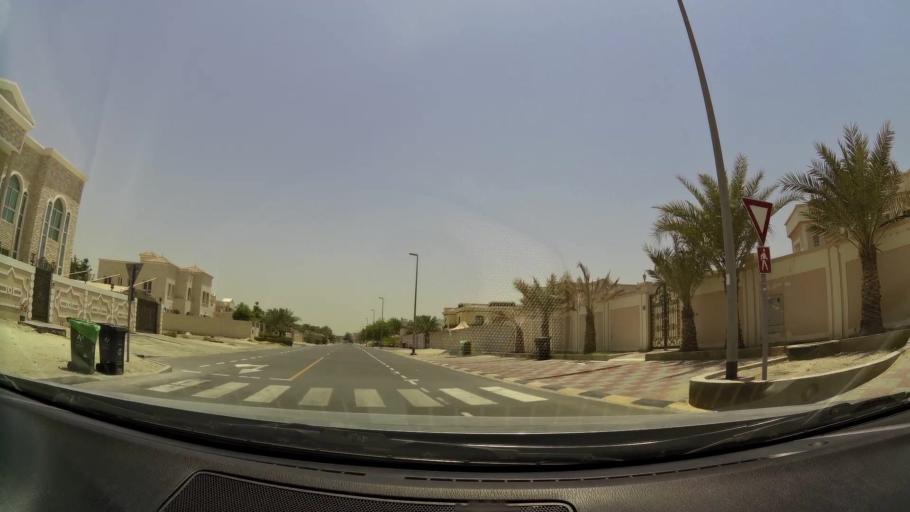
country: AE
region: Dubai
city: Dubai
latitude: 25.0972
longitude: 55.1950
